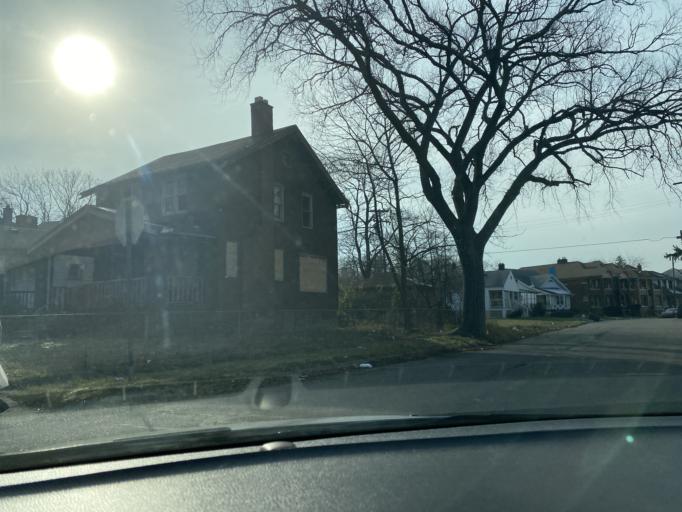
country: US
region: Michigan
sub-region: Wayne County
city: Highland Park
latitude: 42.3756
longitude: -83.1367
